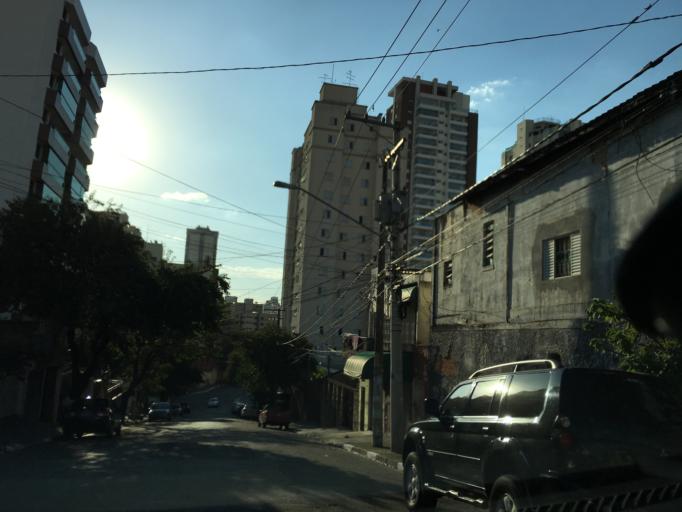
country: BR
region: Sao Paulo
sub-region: Sao Paulo
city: Sao Paulo
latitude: -23.4934
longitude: -46.6367
